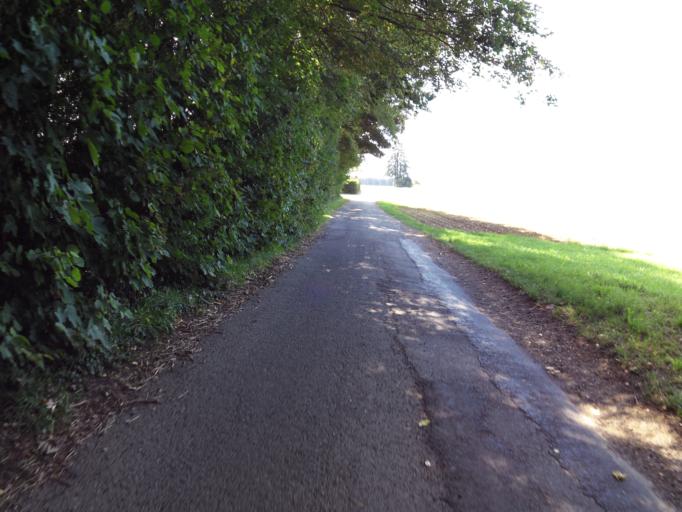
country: DE
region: Baden-Wuerttemberg
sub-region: Freiburg Region
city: Bad Durrheim
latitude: 48.0275
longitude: 8.5025
